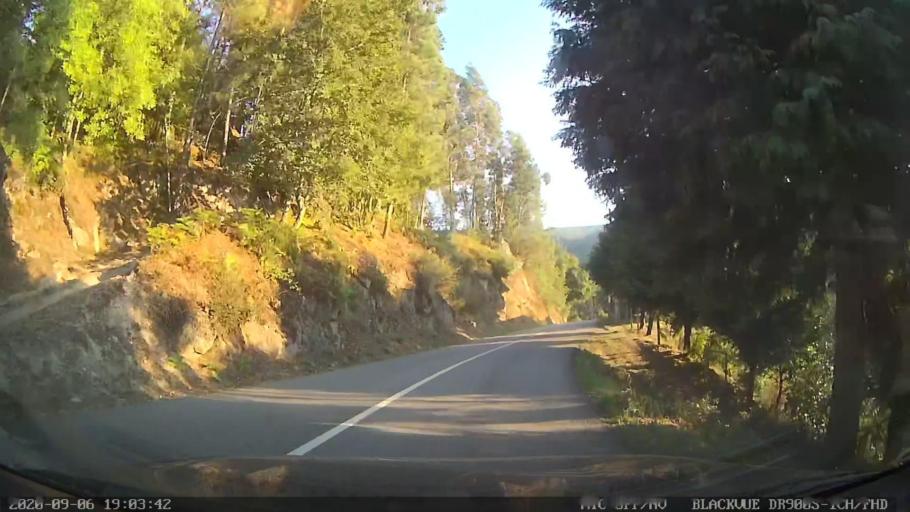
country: PT
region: Porto
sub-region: Baiao
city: Baiao
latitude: 41.2304
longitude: -7.9954
